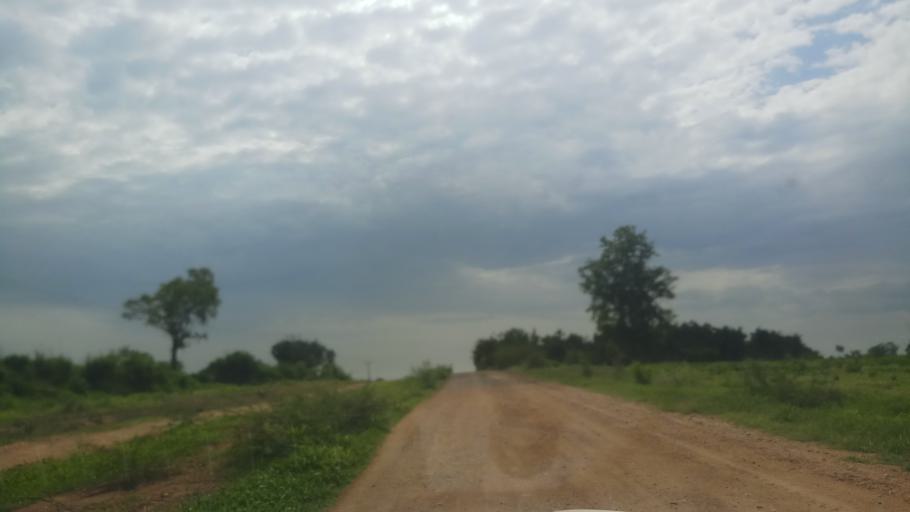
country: ET
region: Gambela
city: Gambela
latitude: 8.2213
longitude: 34.5408
